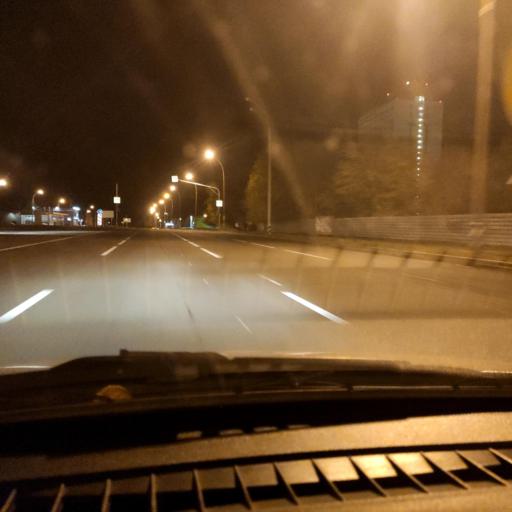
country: RU
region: Samara
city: Tol'yatti
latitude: 53.5035
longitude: 49.2750
